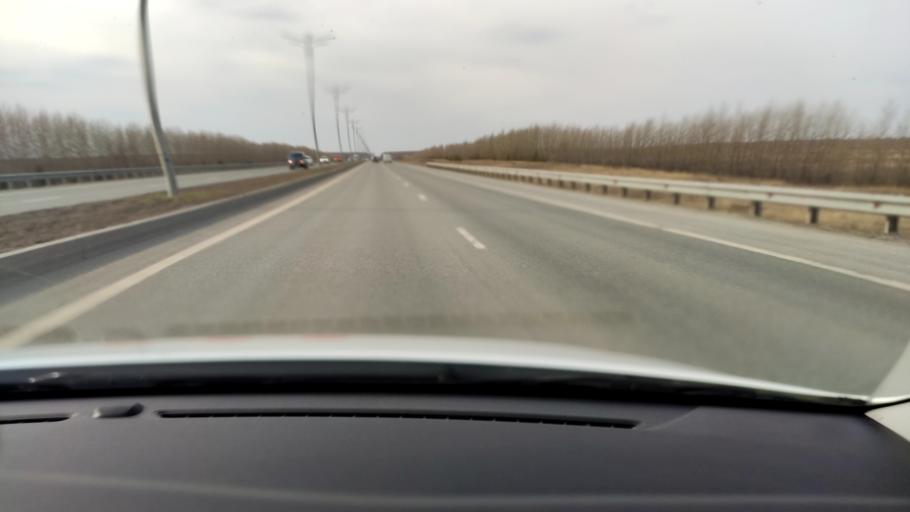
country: RU
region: Tatarstan
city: Stolbishchi
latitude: 55.6848
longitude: 49.2451
